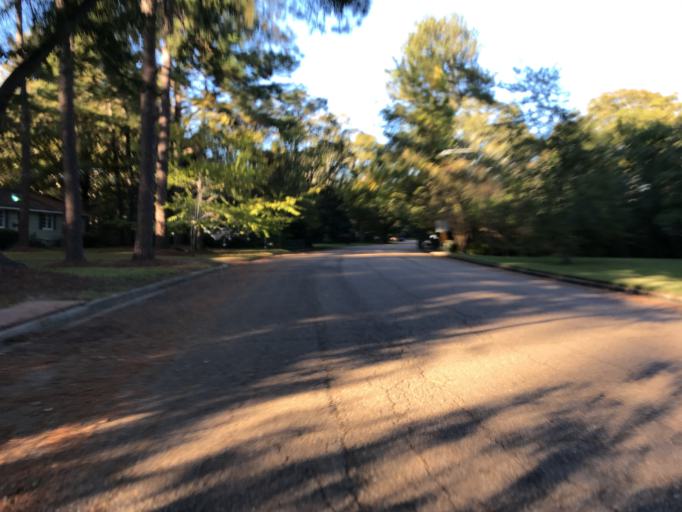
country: US
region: Mississippi
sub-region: Rankin County
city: Flowood
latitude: 32.3432
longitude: -90.1691
